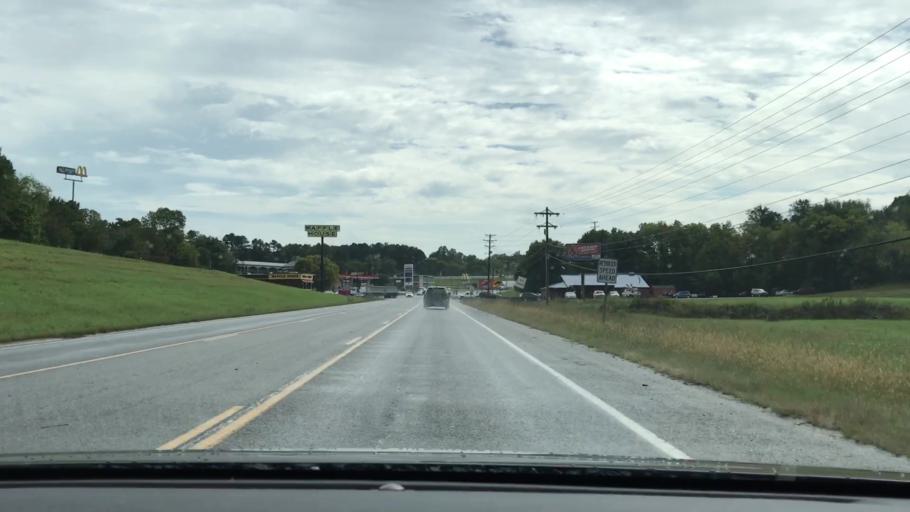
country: US
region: Tennessee
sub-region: Smith County
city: Gordonsville
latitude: 36.1835
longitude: -85.9491
